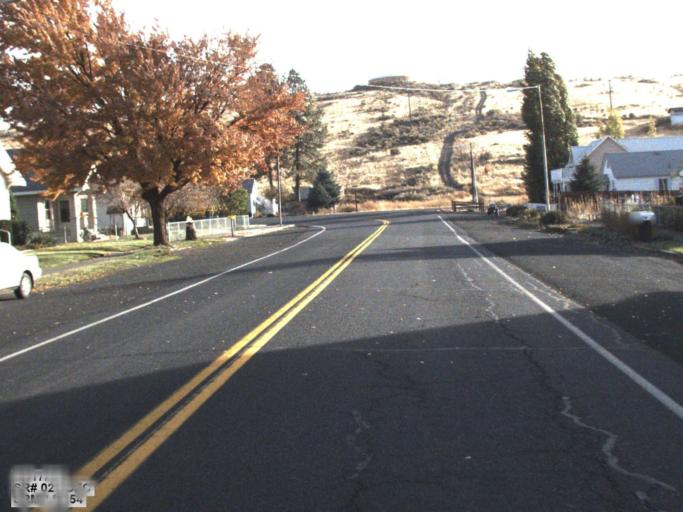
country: US
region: Washington
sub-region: Adams County
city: Ritzville
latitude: 47.3292
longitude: -118.6925
